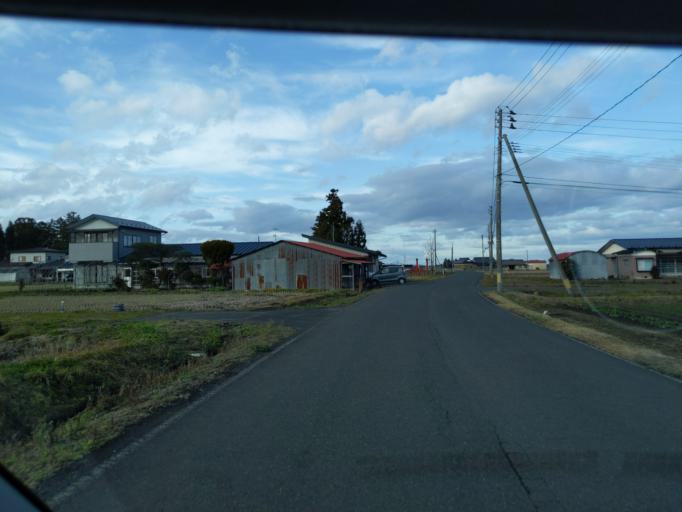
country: JP
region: Iwate
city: Mizusawa
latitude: 39.1488
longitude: 141.0894
